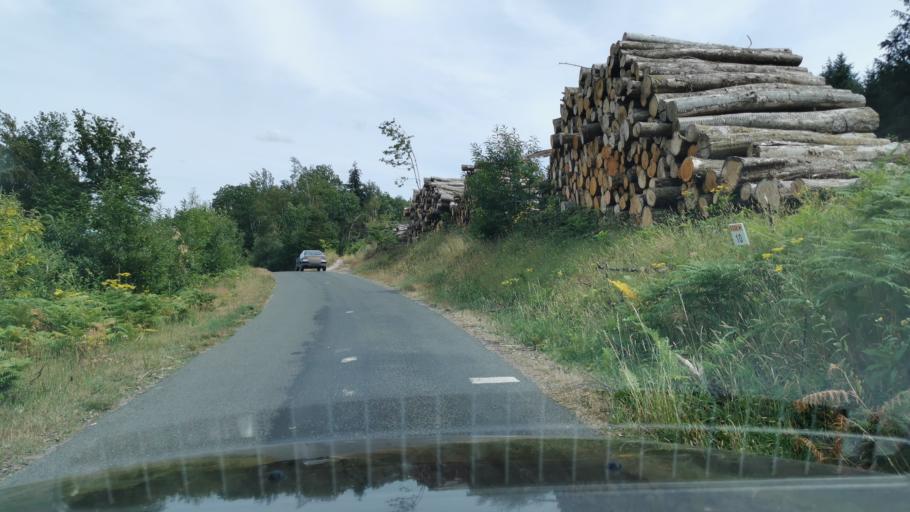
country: FR
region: Bourgogne
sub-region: Departement de Saone-et-Loire
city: Marmagne
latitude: 46.8064
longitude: 4.2883
